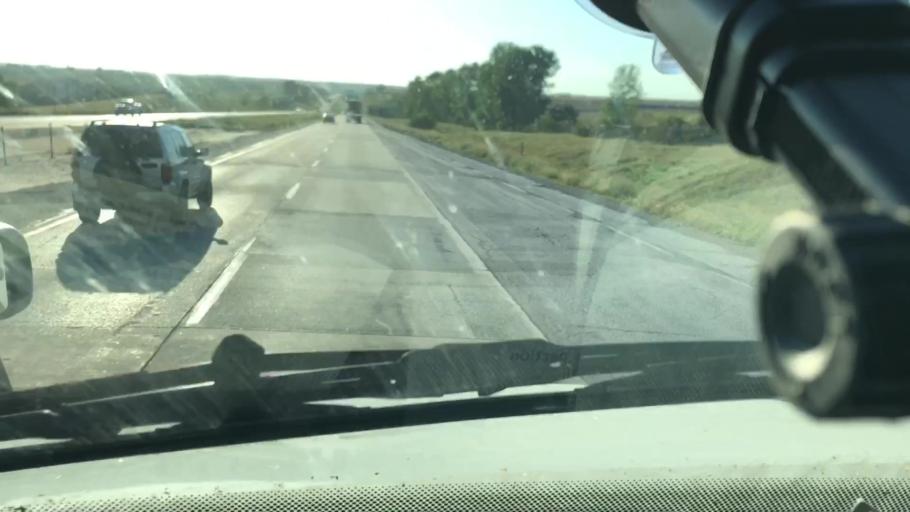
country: US
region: Iowa
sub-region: Pottawattamie County
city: Avoca
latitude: 41.4980
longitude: -95.5521
